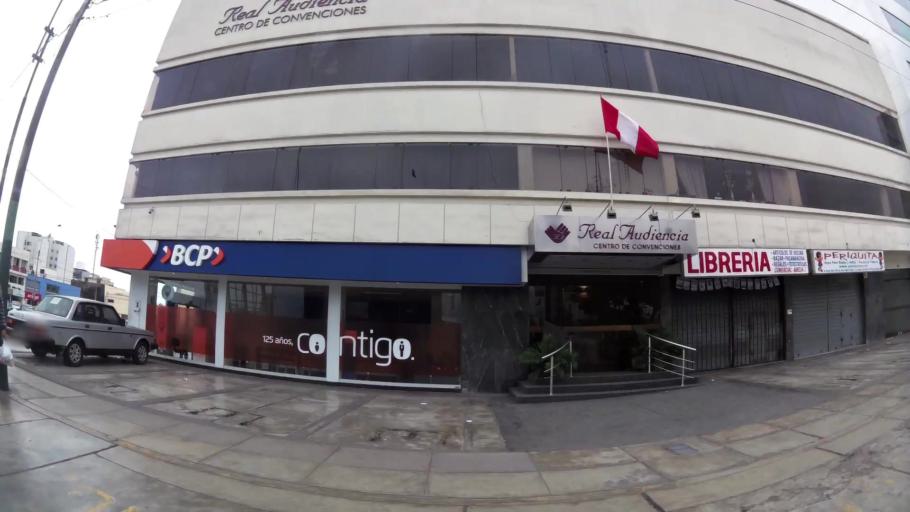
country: PE
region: Lima
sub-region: Lima
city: San Luis
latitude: -12.0985
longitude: -77.0106
